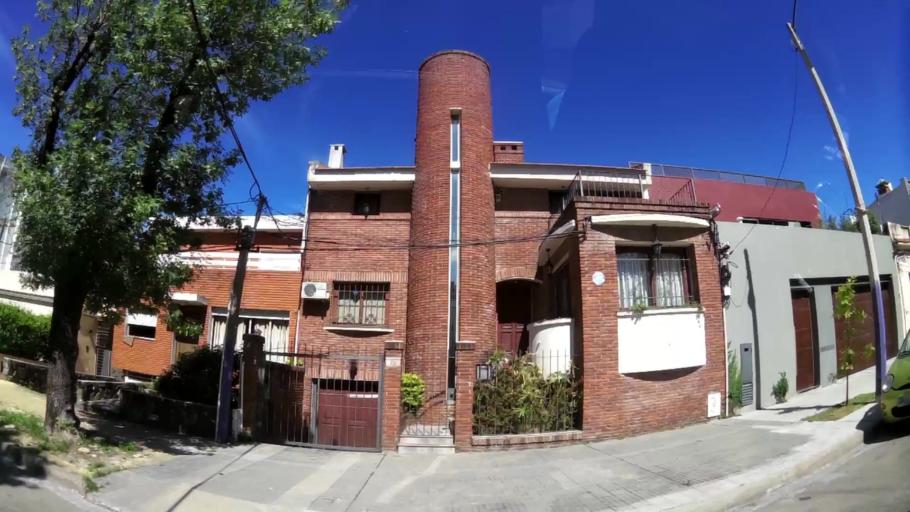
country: UY
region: Montevideo
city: Montevideo
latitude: -34.9171
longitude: -56.1639
